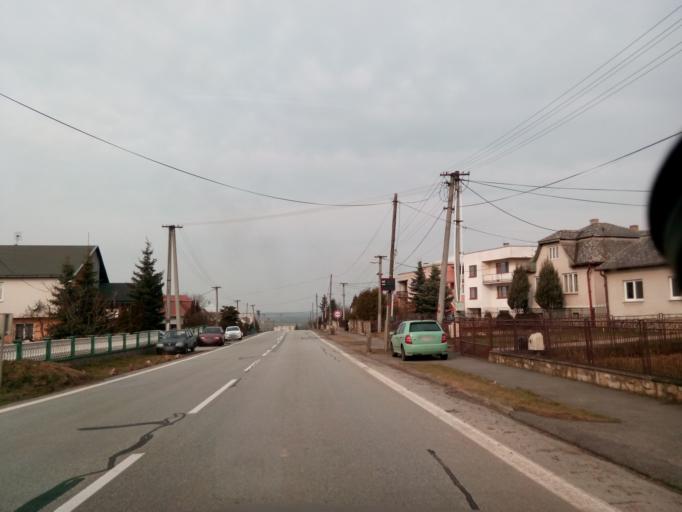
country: HU
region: Borsod-Abauj-Zemplen
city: Satoraljaujhely
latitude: 48.5183
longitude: 21.6598
